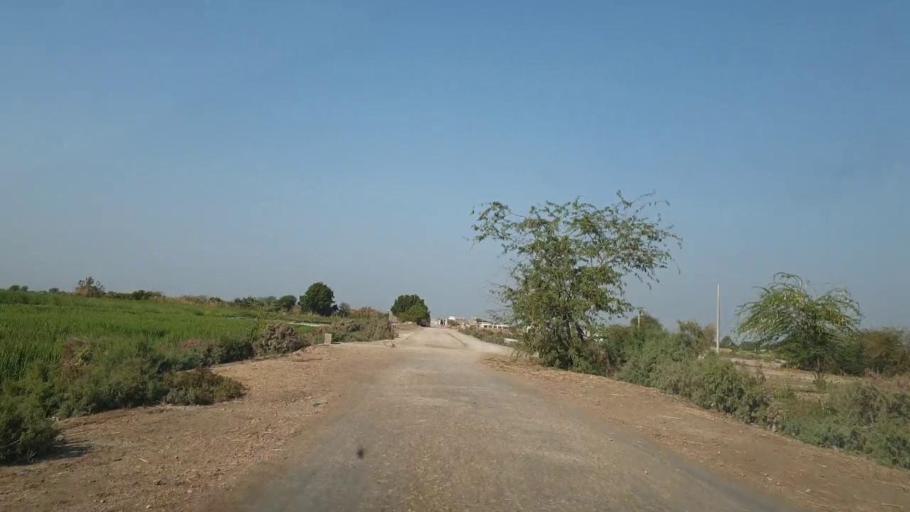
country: PK
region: Sindh
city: Tando Mittha Khan
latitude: 25.7496
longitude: 69.1967
